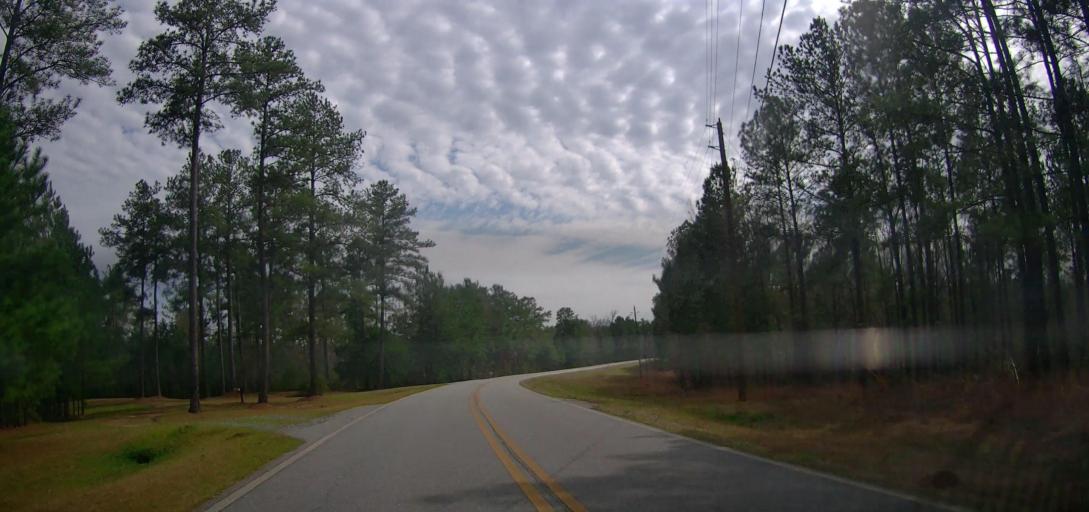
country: US
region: Georgia
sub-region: Jones County
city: Gray
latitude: 33.0253
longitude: -83.7022
